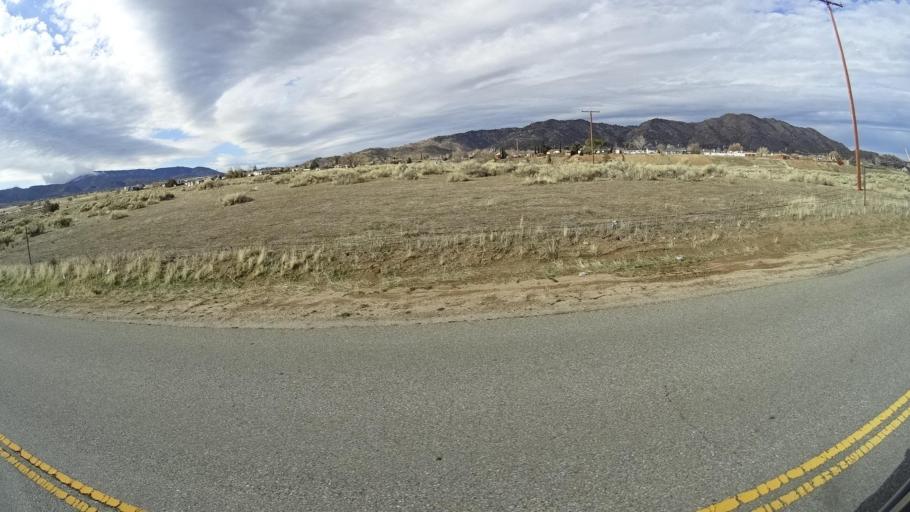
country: US
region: California
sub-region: Kern County
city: Golden Hills
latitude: 35.1278
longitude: -118.4766
